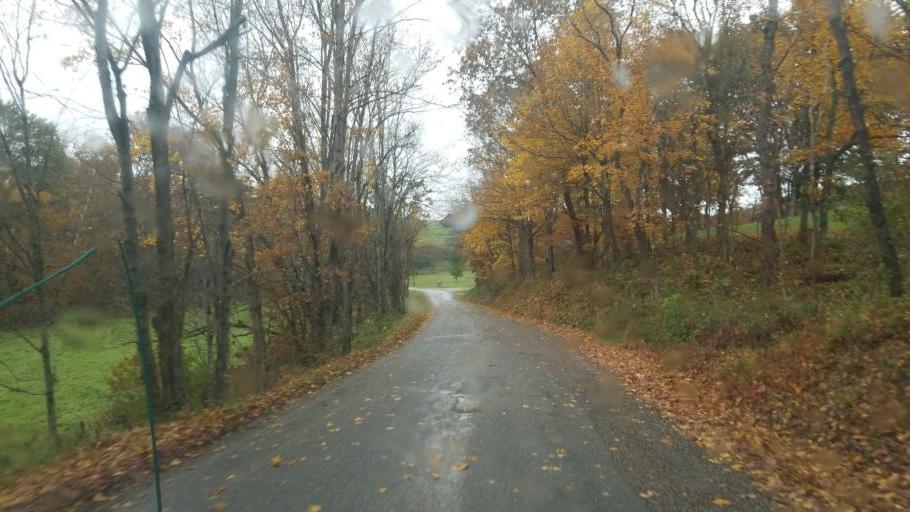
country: US
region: Ohio
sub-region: Washington County
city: Belpre
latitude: 39.3157
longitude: -81.6040
